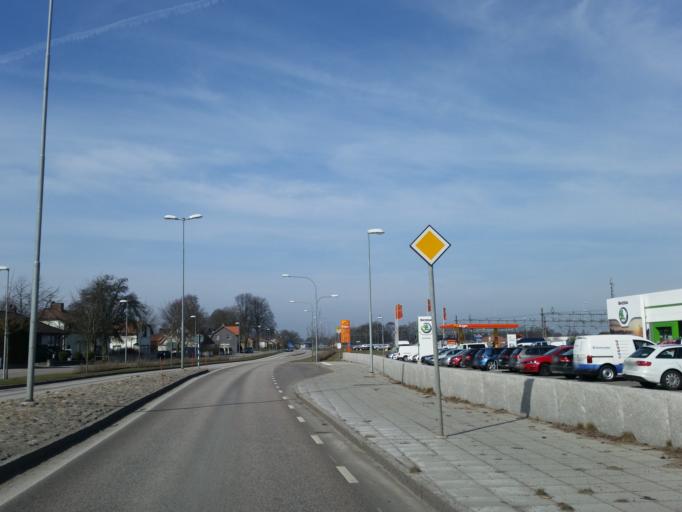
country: SE
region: Kalmar
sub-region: Kalmar Kommun
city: Kalmar
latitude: 56.6660
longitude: 16.3290
